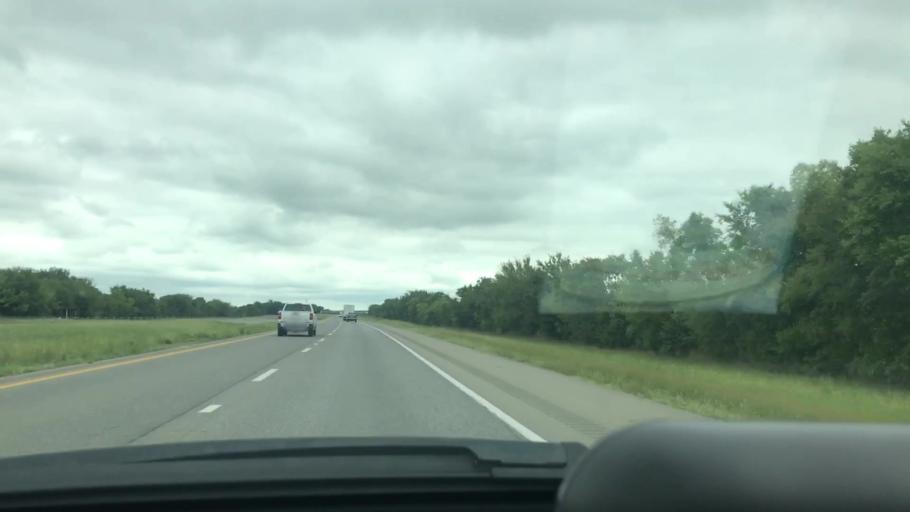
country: US
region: Oklahoma
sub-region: McIntosh County
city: Eufaula
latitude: 35.3803
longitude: -95.5682
